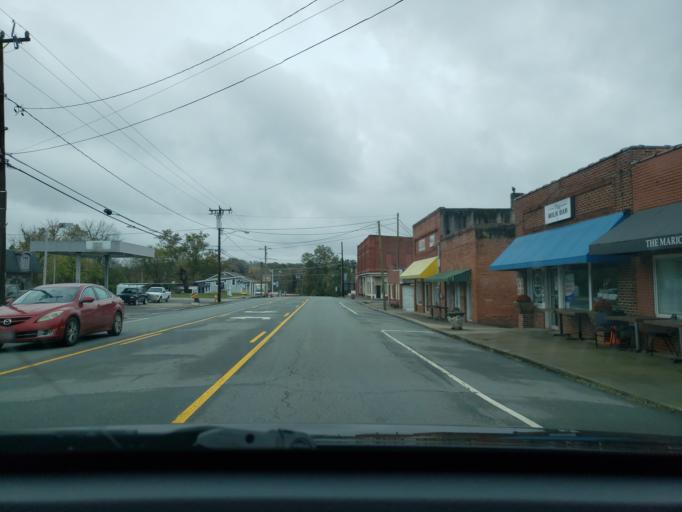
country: US
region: North Carolina
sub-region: Stokes County
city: Walnut Cove
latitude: 36.2949
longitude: -80.1418
